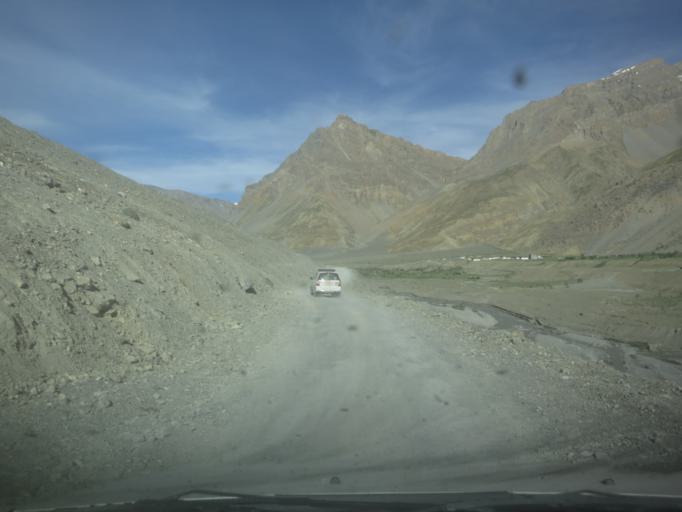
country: IN
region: Himachal Pradesh
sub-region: Kulu
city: Manali
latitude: 32.4382
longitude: 77.8129
